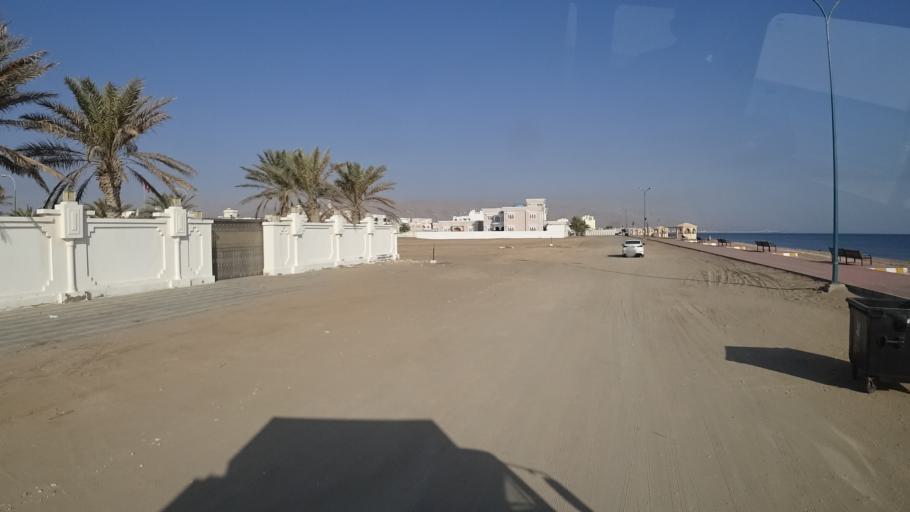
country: OM
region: Ash Sharqiyah
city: Sur
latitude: 22.5937
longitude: 59.4981
